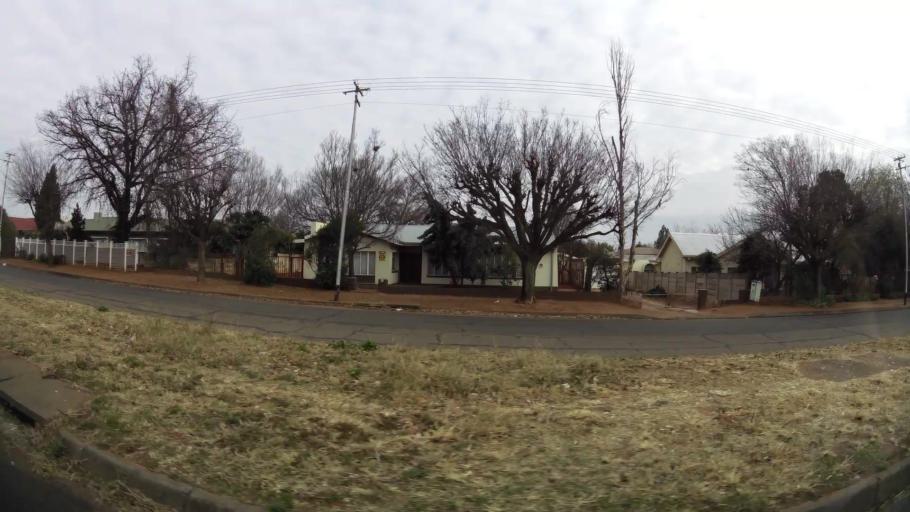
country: ZA
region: Orange Free State
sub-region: Mangaung Metropolitan Municipality
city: Bloemfontein
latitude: -29.1448
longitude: 26.1945
